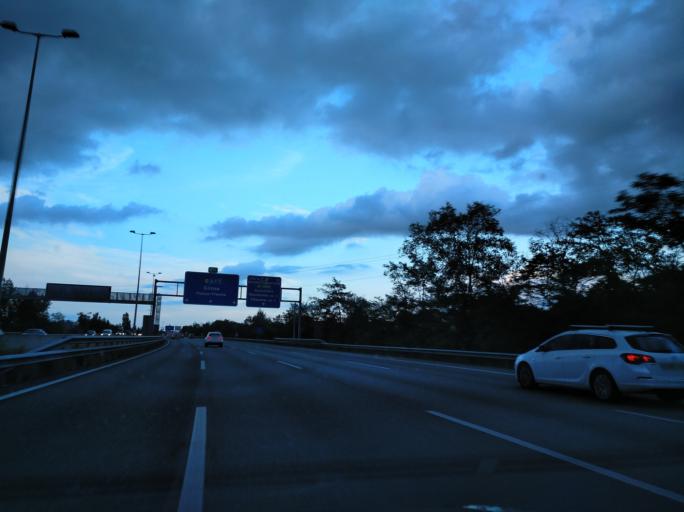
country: ES
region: Catalonia
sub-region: Provincia de Barcelona
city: Montornes del Valles
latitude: 41.5614
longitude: 2.2699
